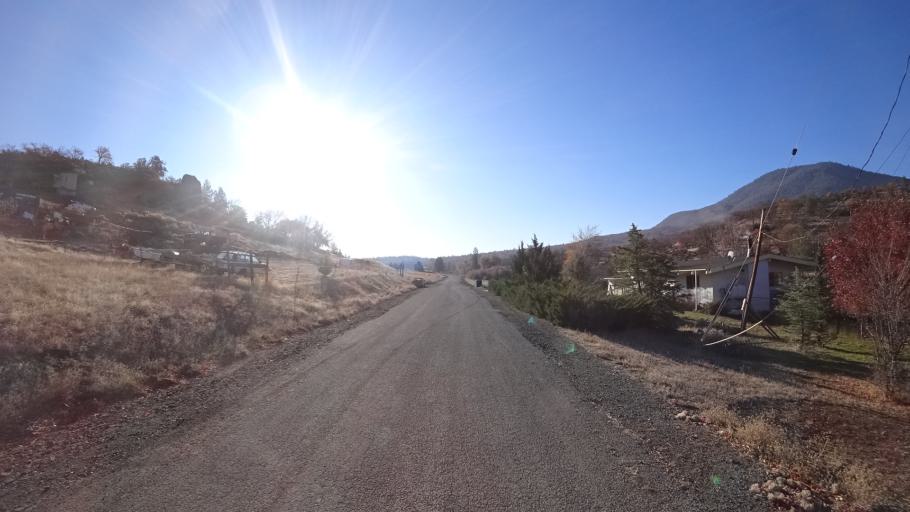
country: US
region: California
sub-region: Siskiyou County
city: Montague
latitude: 41.8939
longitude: -122.4937
